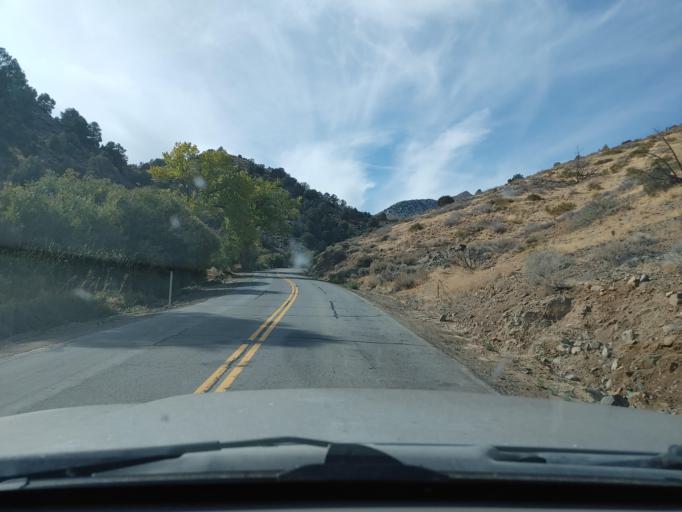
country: US
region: Nevada
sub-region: Storey County
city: Virginia City
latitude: 39.3066
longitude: -119.6251
